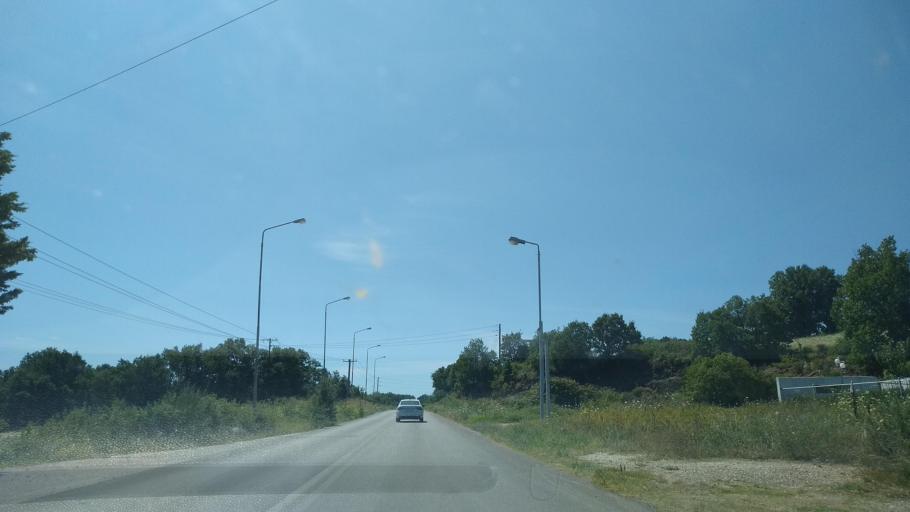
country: GR
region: Central Macedonia
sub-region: Nomos Chalkidikis
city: Megali Panagia
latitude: 40.4185
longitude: 23.6906
